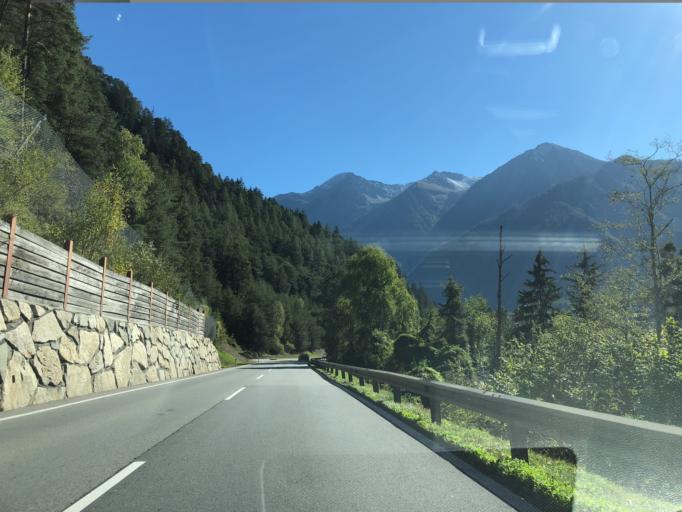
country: AT
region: Tyrol
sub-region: Politischer Bezirk Imst
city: Sautens
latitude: 47.2256
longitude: 10.8609
